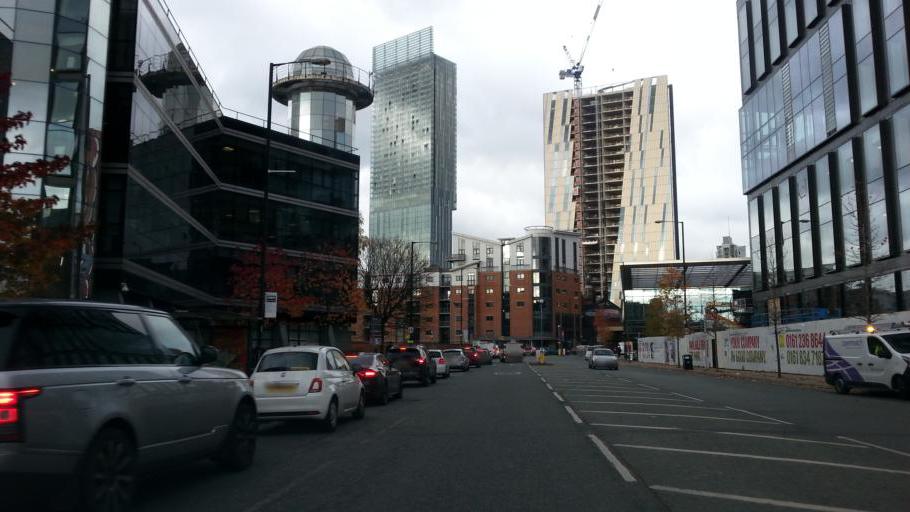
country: GB
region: England
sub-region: Manchester
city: Hulme
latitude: 53.4723
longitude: -2.2478
